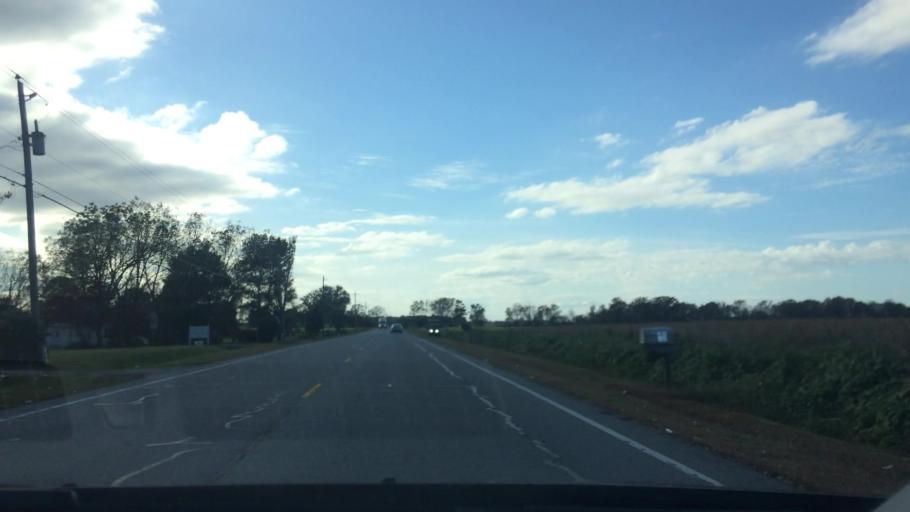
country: US
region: North Carolina
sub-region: Greene County
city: Snow Hill
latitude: 35.4377
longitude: -77.7629
